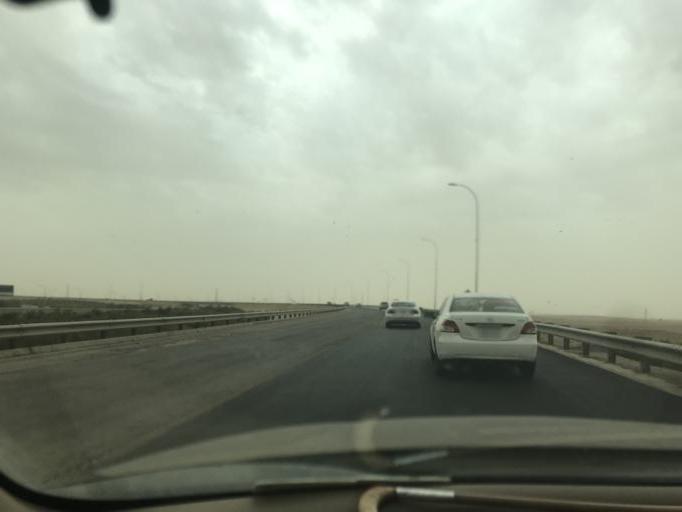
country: SA
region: Ar Riyad
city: Riyadh
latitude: 24.9085
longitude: 46.7152
